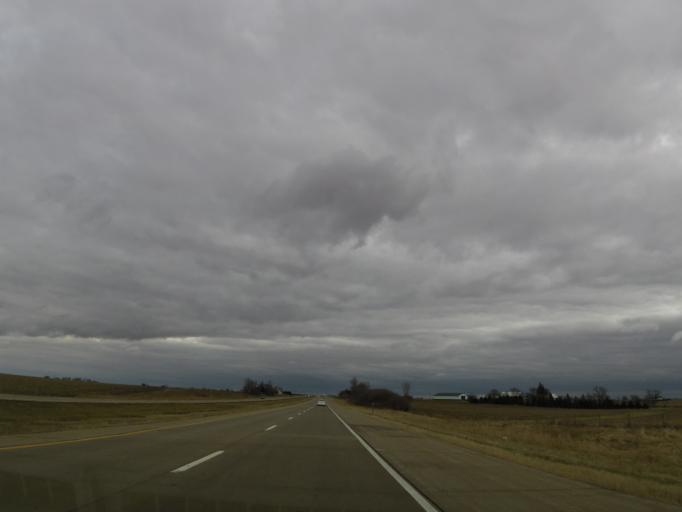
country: US
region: Iowa
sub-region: Black Hawk County
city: La Porte City
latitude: 42.4033
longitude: -92.1570
